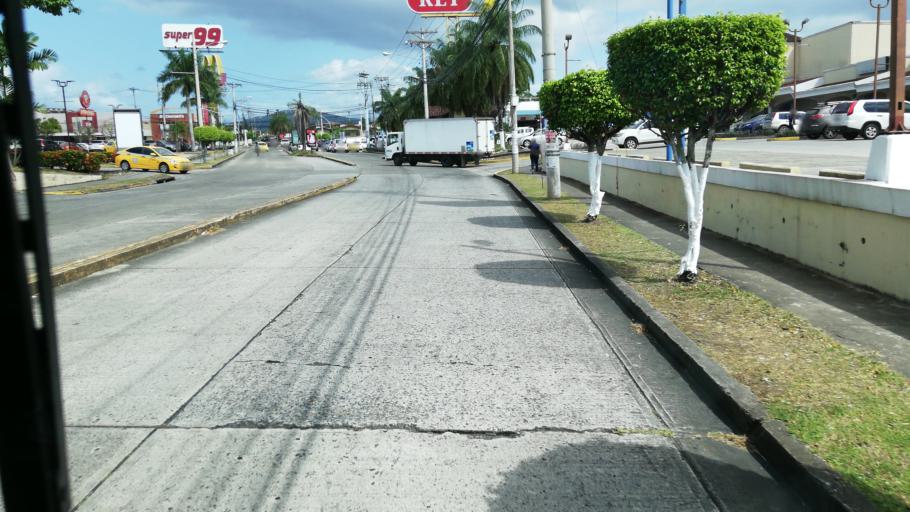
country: PA
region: Panama
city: San Miguelito
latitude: 9.0685
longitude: -79.4524
